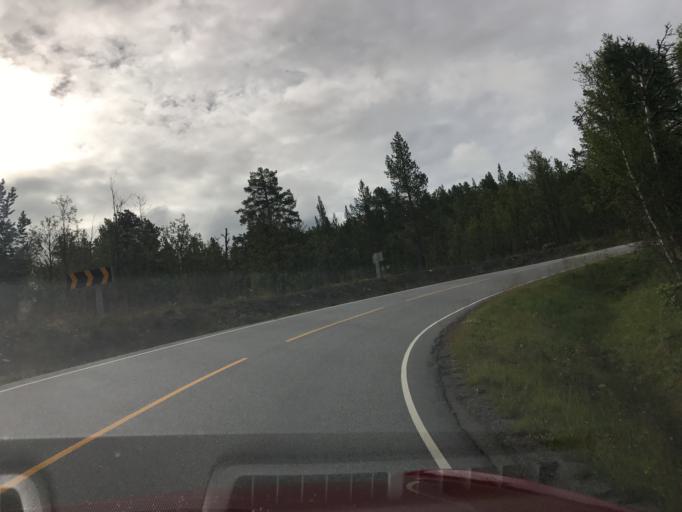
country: NO
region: Buskerud
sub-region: Al
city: Al
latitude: 60.4011
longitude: 8.4537
